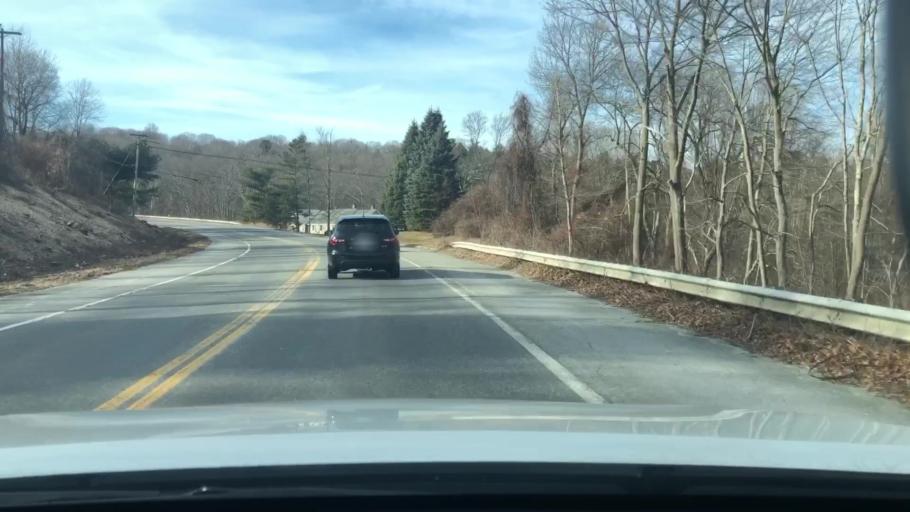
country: US
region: Massachusetts
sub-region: Worcester County
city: Grafton
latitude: 42.2049
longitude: -71.6648
